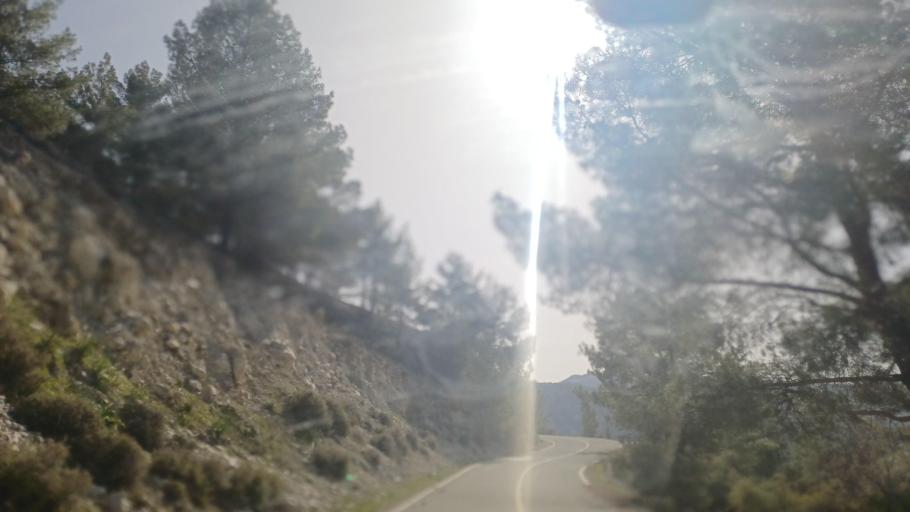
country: CY
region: Limassol
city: Pachna
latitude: 34.8809
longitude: 32.7297
